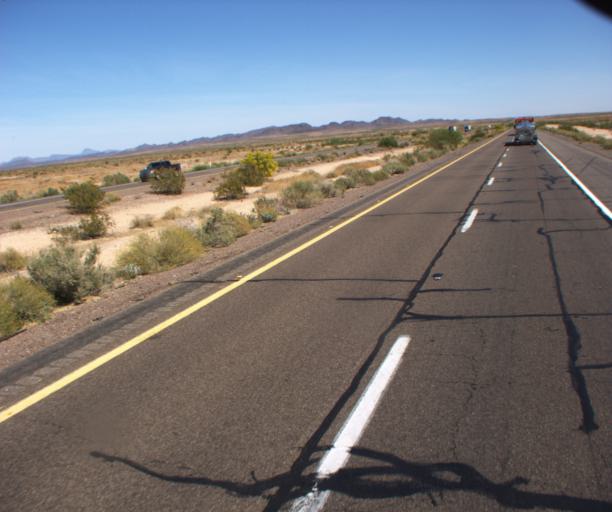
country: US
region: Arizona
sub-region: Maricopa County
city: Gila Bend
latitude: 32.8783
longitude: -113.1118
